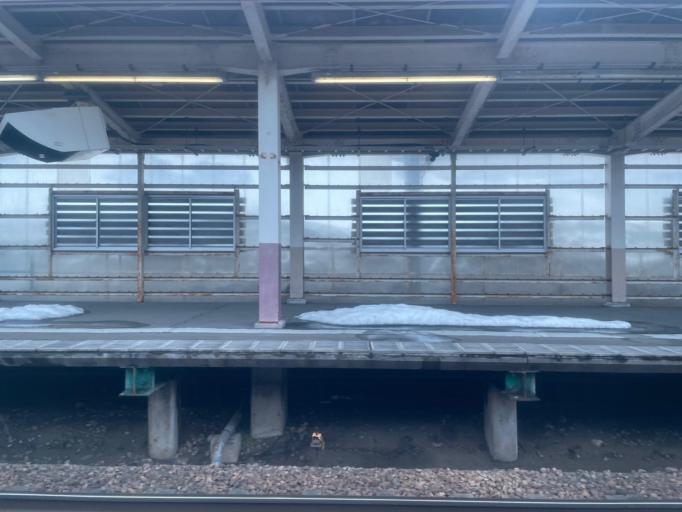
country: JP
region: Niigata
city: Shiozawa
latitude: 36.9351
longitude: 138.8109
